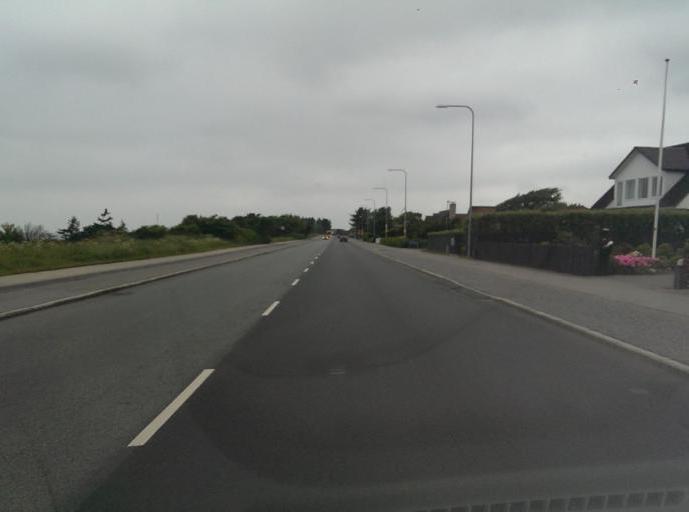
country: DK
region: South Denmark
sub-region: Fano Kommune
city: Nordby
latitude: 55.4985
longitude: 8.3947
